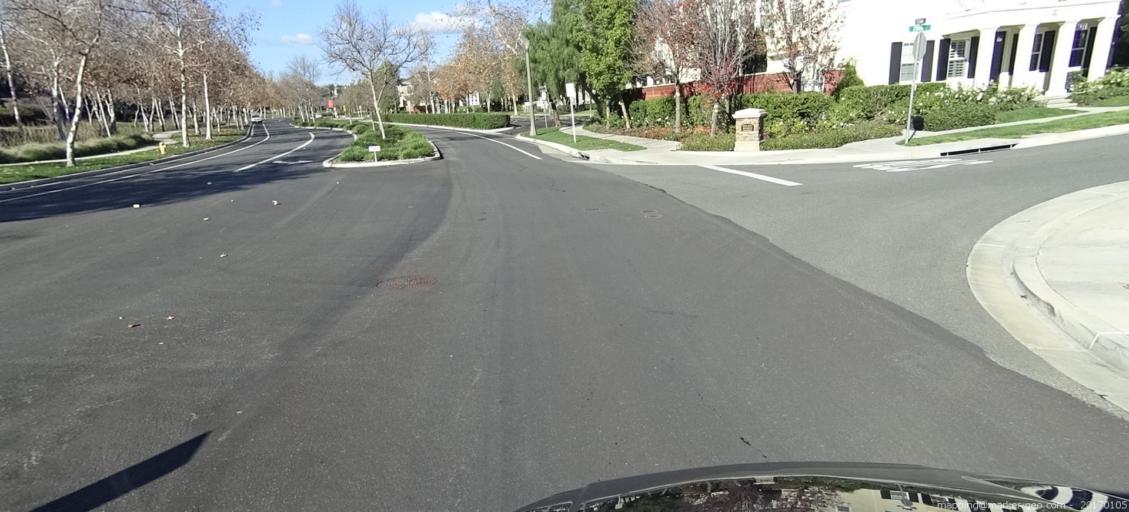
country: US
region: California
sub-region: Orange County
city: Ladera Ranch
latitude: 33.5485
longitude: -117.6376
